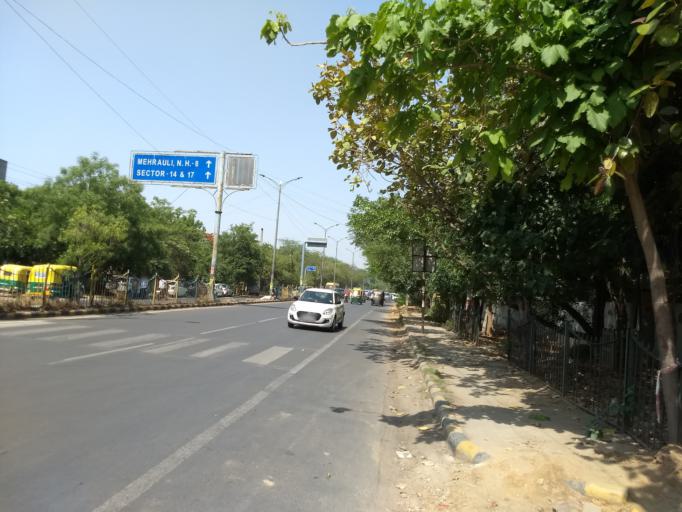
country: IN
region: Haryana
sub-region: Gurgaon
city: Gurgaon
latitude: 28.4708
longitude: 77.0486
